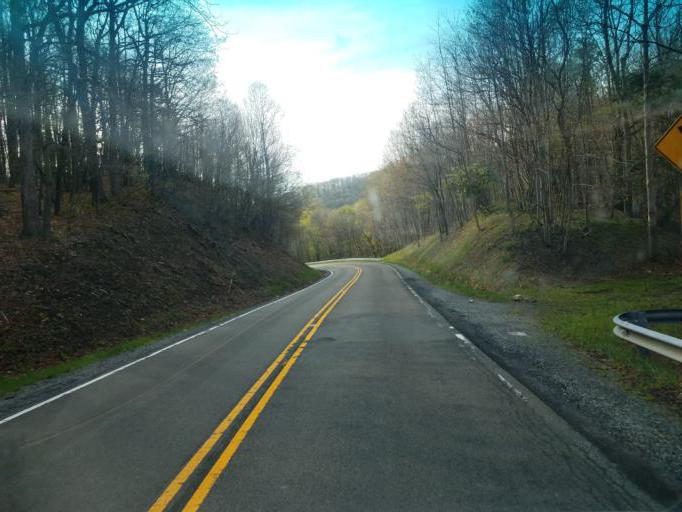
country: US
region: Virginia
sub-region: Smyth County
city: Atkins
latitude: 36.8110
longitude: -81.4186
